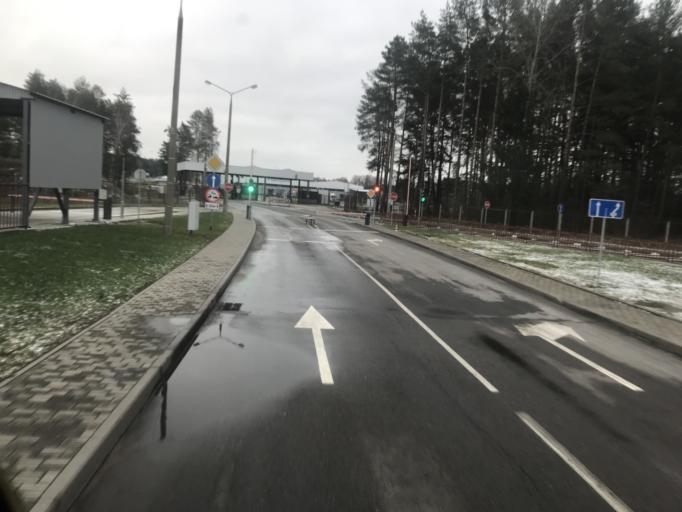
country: BY
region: Grodnenskaya
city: Vyalikaya Byerastavitsa
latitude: 53.1208
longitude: 23.8992
